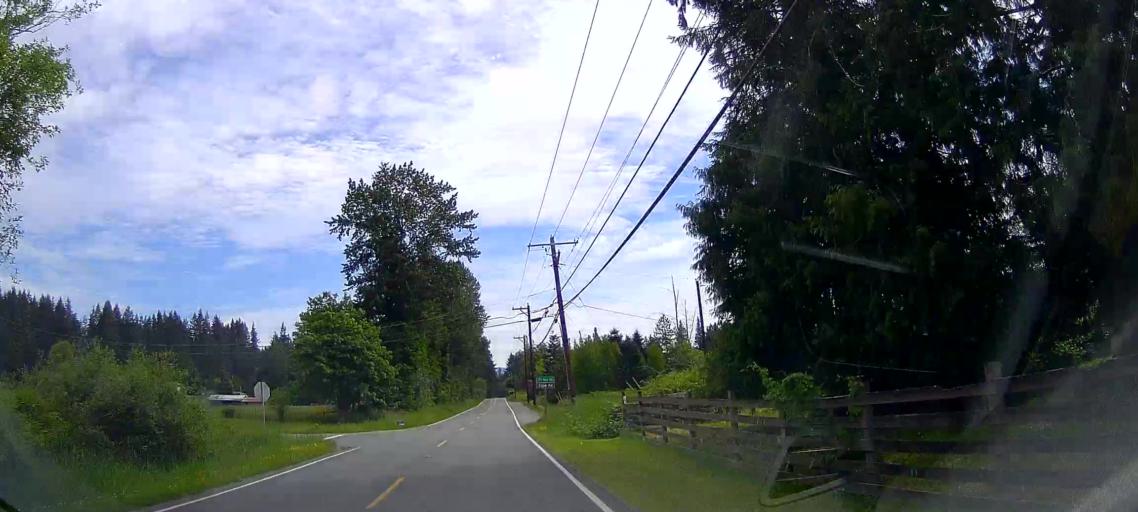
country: US
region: Washington
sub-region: Snohomish County
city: Bryant
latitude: 48.2388
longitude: -122.1830
